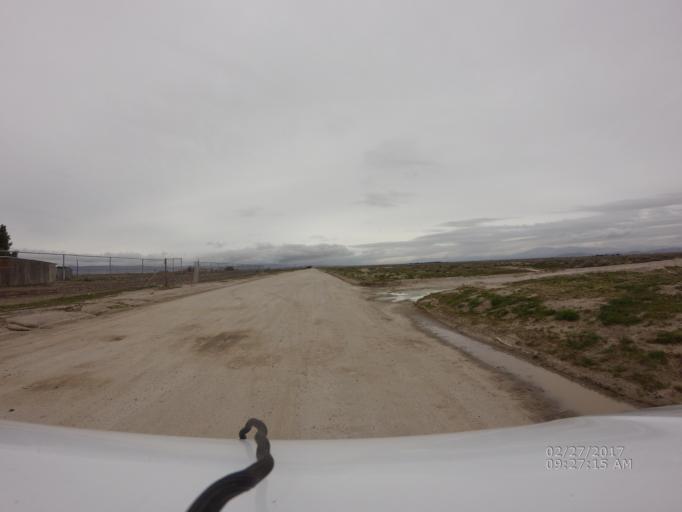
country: US
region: California
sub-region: Los Angeles County
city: Lancaster
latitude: 34.7480
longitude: -118.1313
